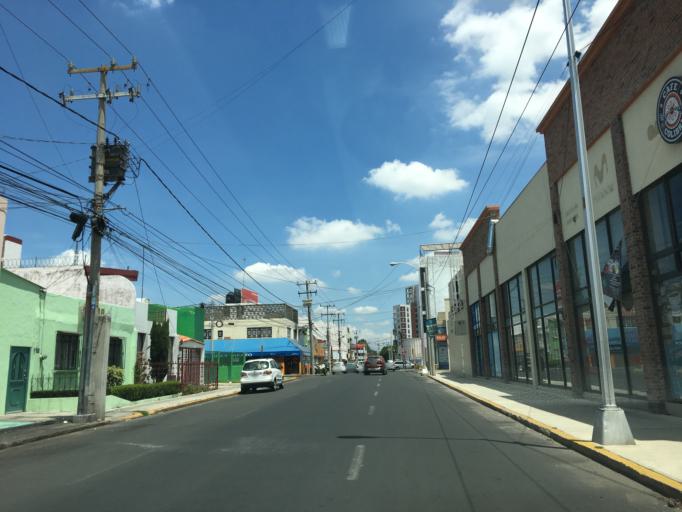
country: MX
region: Puebla
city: Puebla
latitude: 19.0554
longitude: -98.2201
